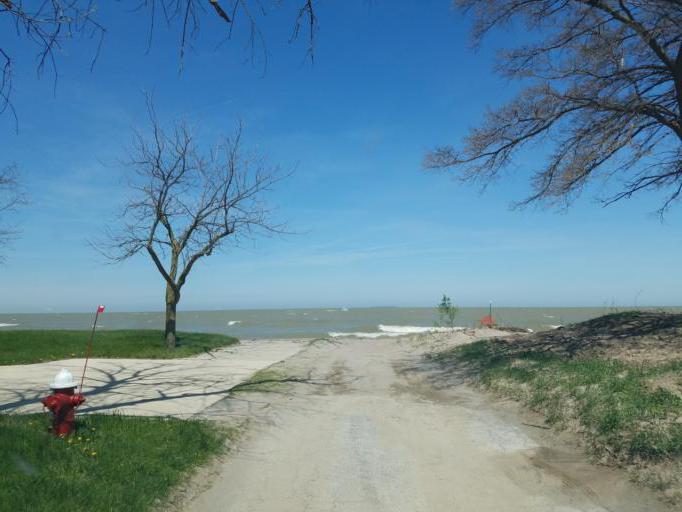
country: US
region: Ohio
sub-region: Ottawa County
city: Oak Harbor
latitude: 41.6128
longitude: -83.1052
